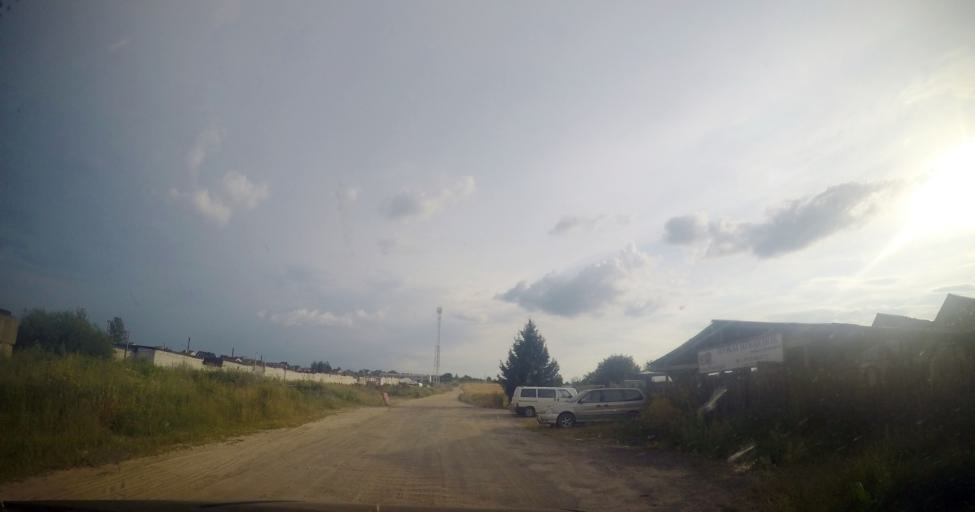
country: BY
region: Grodnenskaya
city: Hrodna
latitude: 53.6232
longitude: 23.8367
